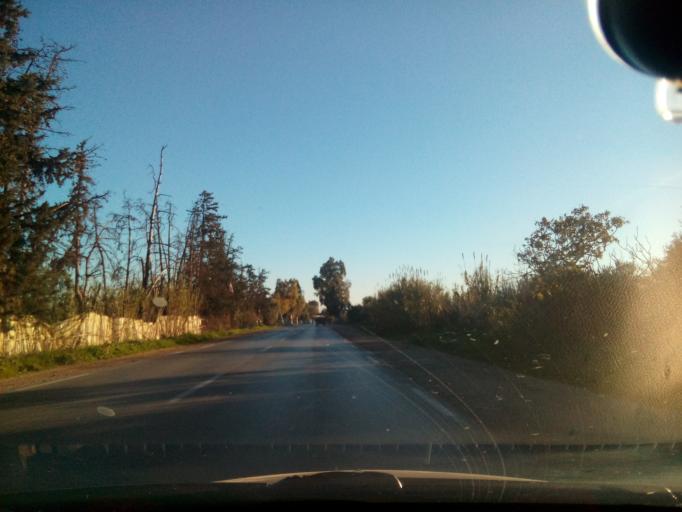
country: DZ
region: Mostaganem
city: Mostaganem
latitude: 35.8039
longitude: 0.1718
